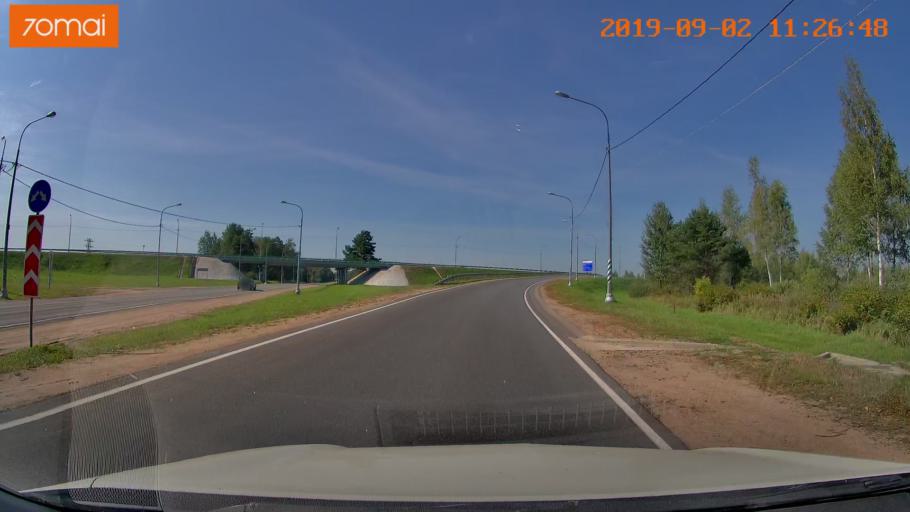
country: RU
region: Smolensk
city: Roslavl'
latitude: 53.9903
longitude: 32.9255
